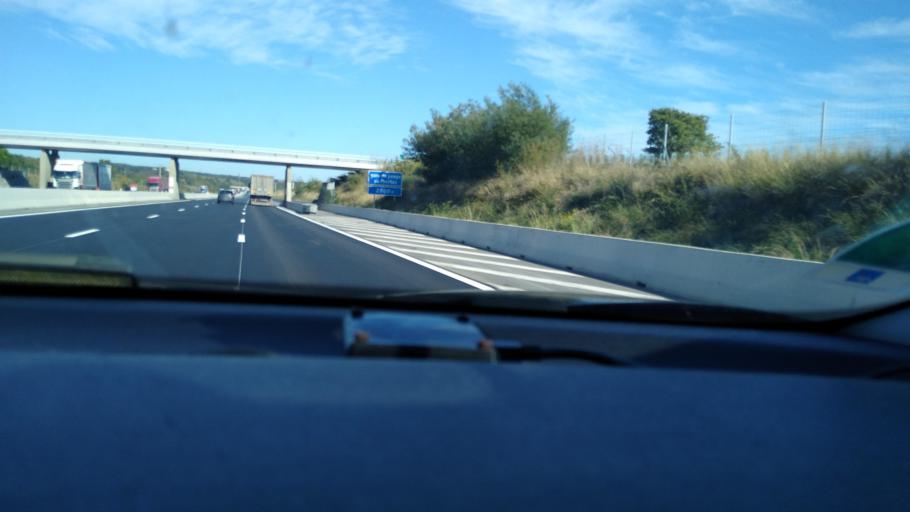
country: FR
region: Languedoc-Roussillon
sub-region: Departement des Pyrenees-Orientales
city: el Volo
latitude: 42.5096
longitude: 2.8183
